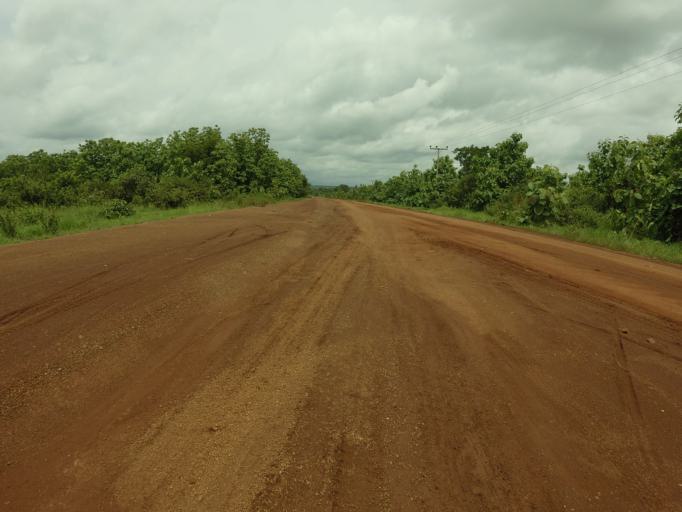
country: GH
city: Kpandae
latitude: 8.4097
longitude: 0.3949
